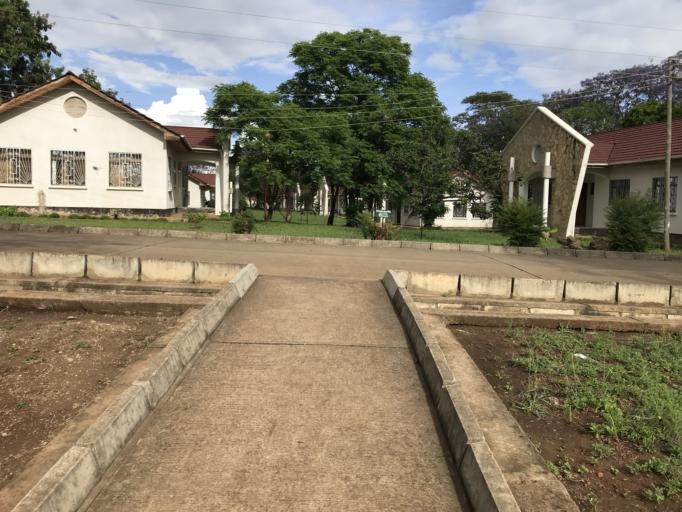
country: TZ
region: Arusha
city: Usa River
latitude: -3.4003
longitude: 36.7981
